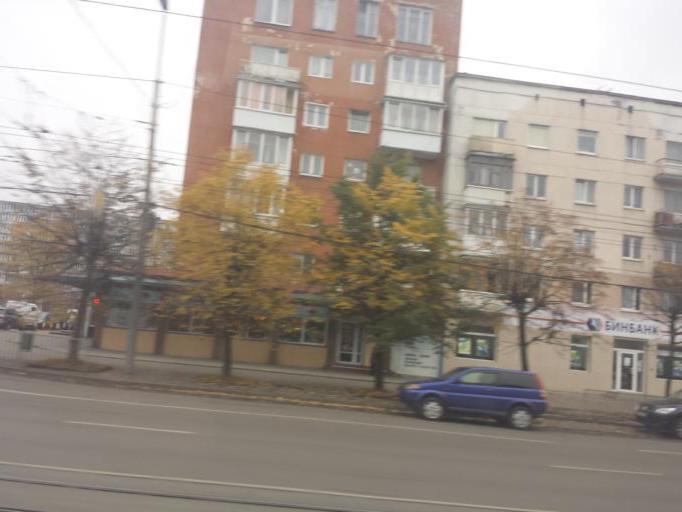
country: RU
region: Kaliningrad
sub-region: Gorod Kaliningrad
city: Kaliningrad
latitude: 54.7040
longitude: 20.5056
